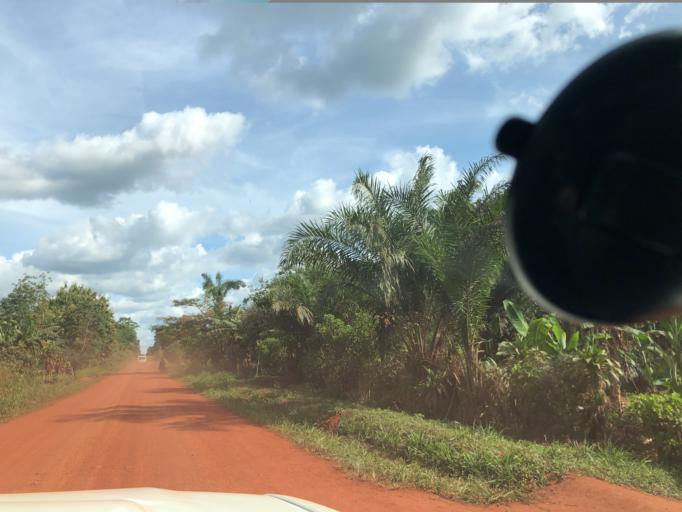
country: CD
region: Equateur
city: Gemena
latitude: 2.9811
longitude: 19.8995
